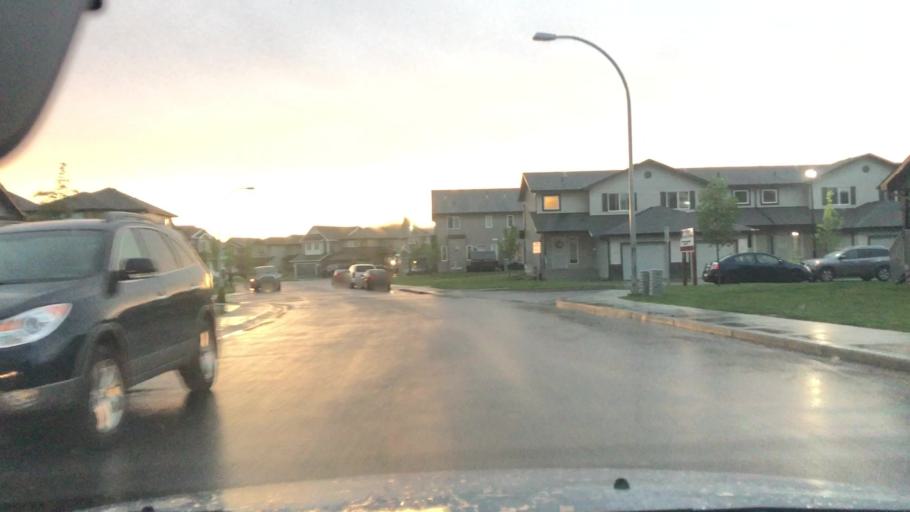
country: CA
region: Alberta
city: St. Albert
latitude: 53.6277
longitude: -113.5601
